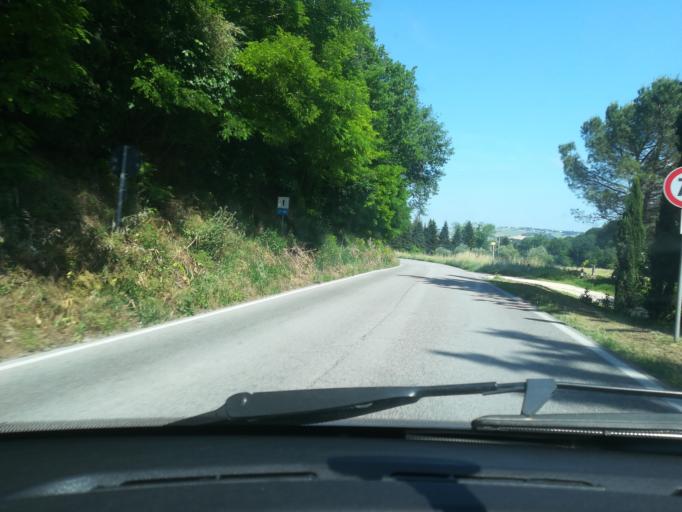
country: IT
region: The Marches
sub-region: Provincia di Macerata
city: Passo di Treia
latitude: 43.2925
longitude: 13.3248
